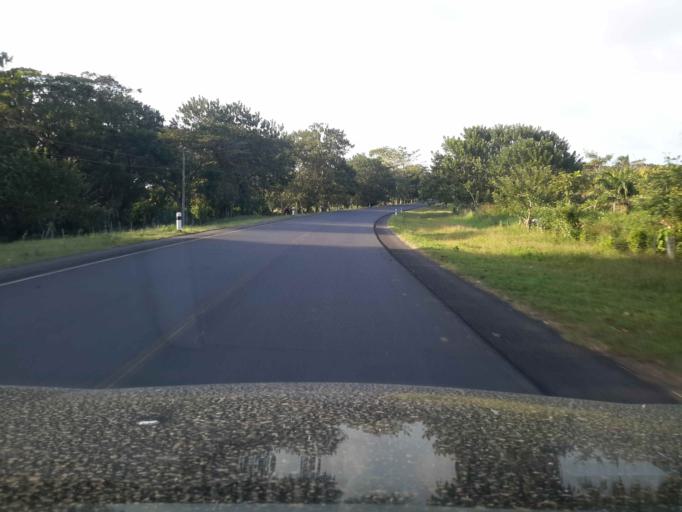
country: NI
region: Rio San Juan
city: San Carlos
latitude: 11.2926
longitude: -84.7255
